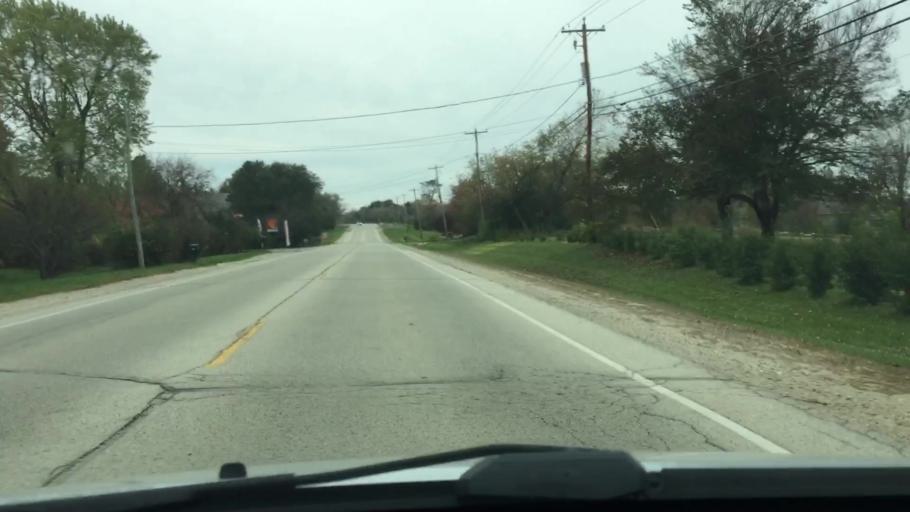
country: US
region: Wisconsin
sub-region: Waukesha County
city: Muskego
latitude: 42.9400
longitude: -88.1673
